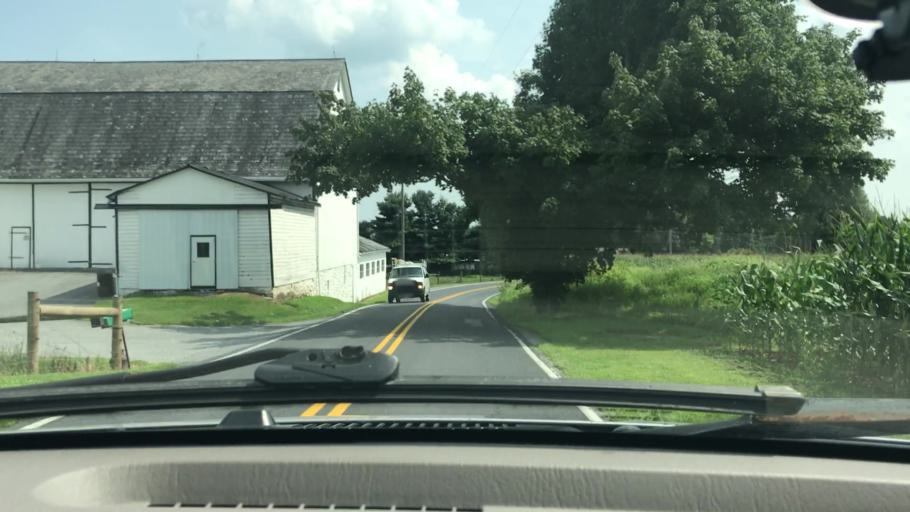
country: US
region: Pennsylvania
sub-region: Lancaster County
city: Rheems
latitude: 40.1489
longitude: -76.5714
